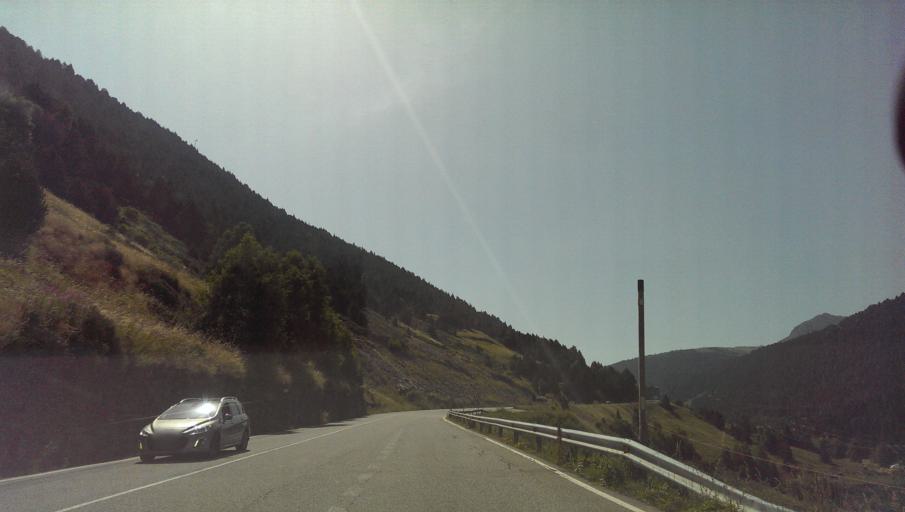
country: AD
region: Canillo
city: El Tarter
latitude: 42.5707
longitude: 1.6775
